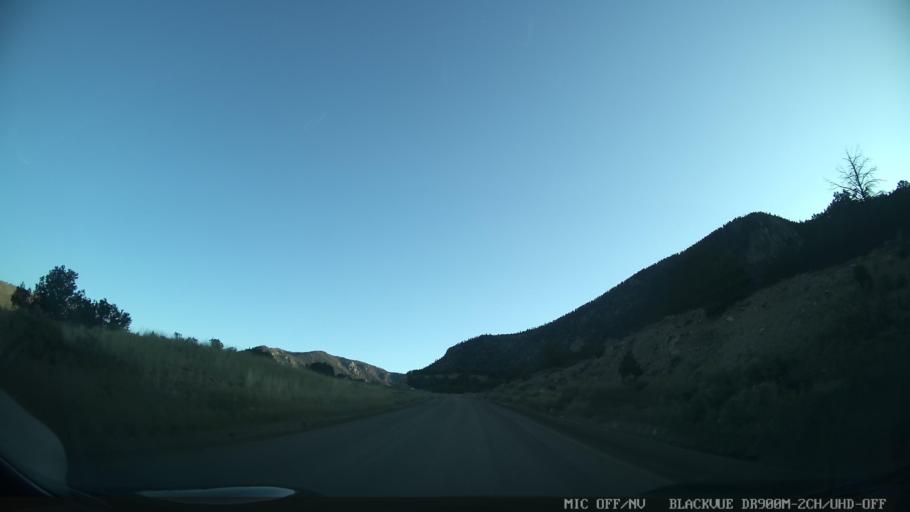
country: US
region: Colorado
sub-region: Grand County
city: Kremmling
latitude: 39.9844
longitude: -106.4945
